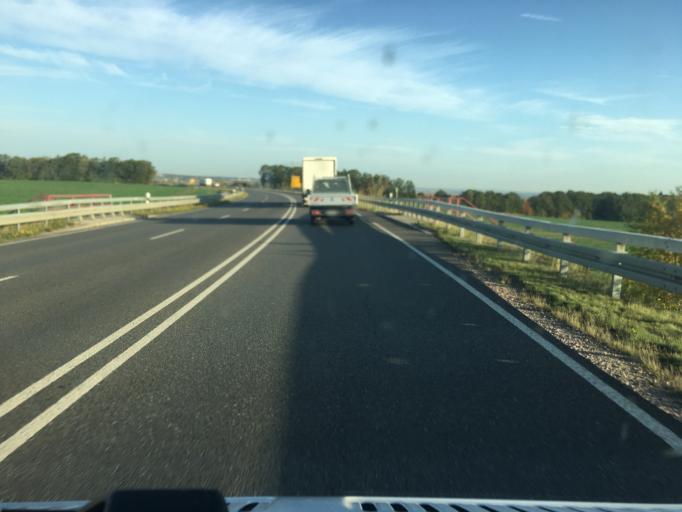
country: DE
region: Saxony
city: Lichtentanne
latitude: 50.6783
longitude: 12.4477
